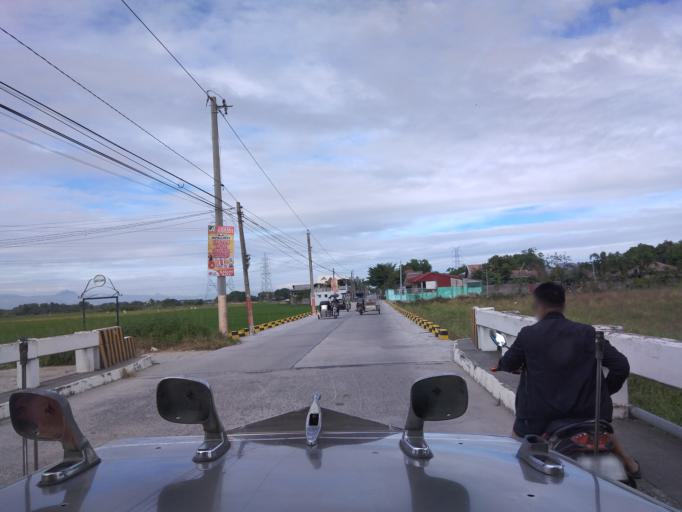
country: PH
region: Central Luzon
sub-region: Province of Pampanga
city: Mexico
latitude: 15.0704
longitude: 120.7141
